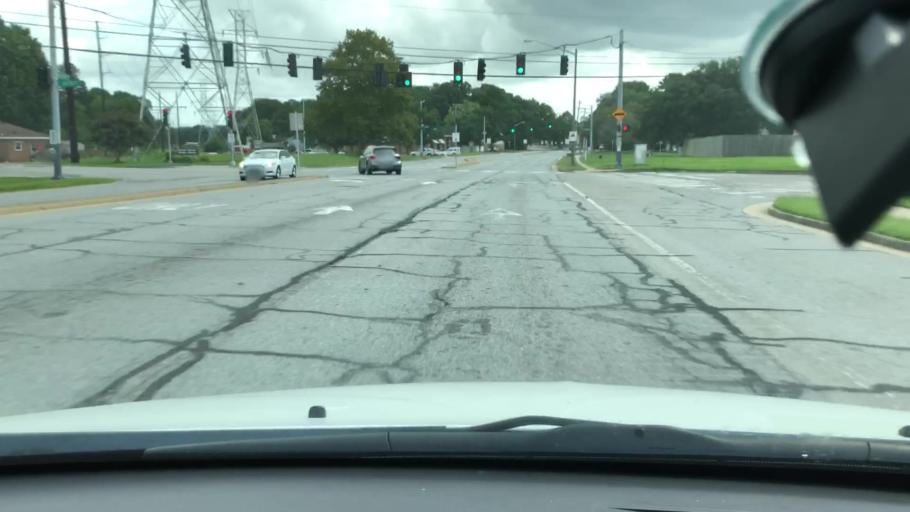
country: US
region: Virginia
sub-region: City of Chesapeake
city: Chesapeake
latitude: 36.8139
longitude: -76.1909
